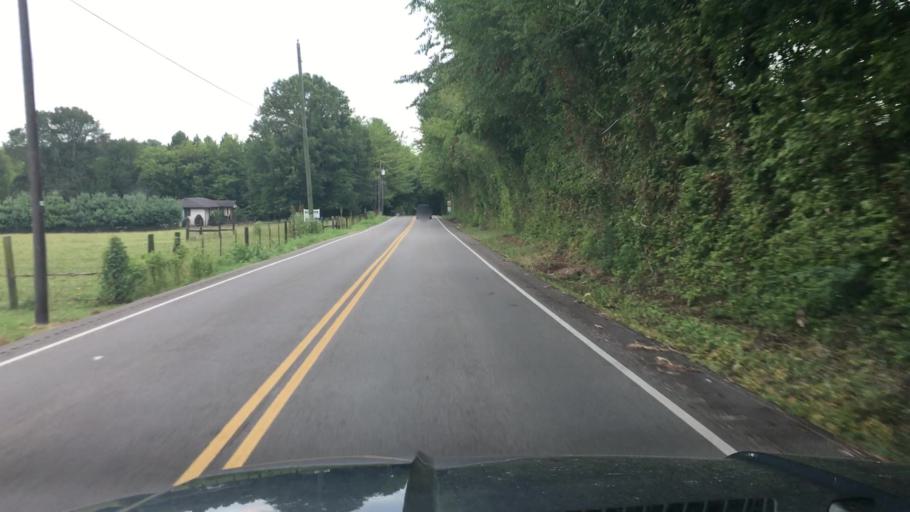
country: US
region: Tennessee
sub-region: Williamson County
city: Thompson's Station
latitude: 35.8065
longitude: -86.8625
